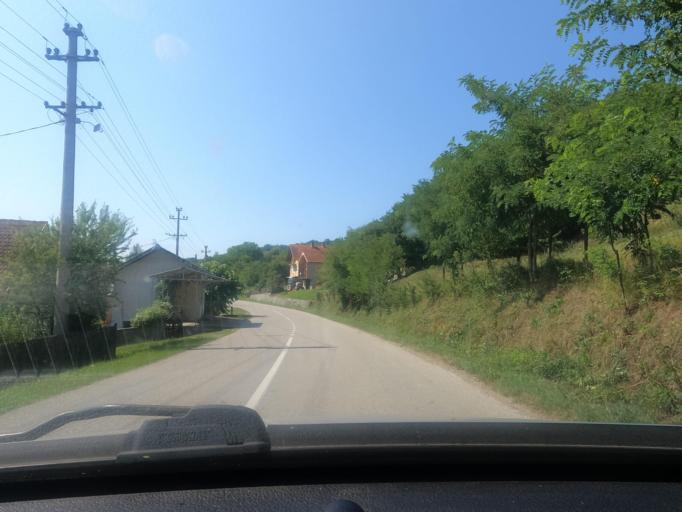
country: RS
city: Jadranska Lesnica
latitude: 44.5494
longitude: 19.3411
